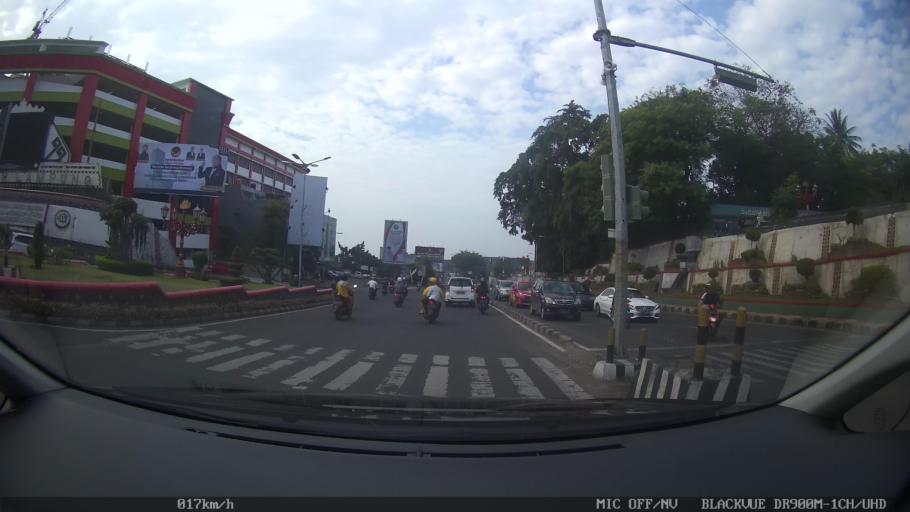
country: ID
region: Lampung
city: Bandarlampung
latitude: -5.4295
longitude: 105.2614
